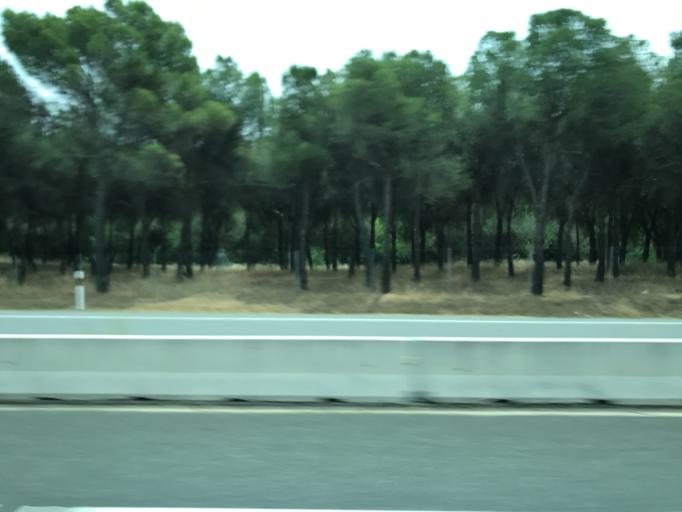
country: ES
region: Madrid
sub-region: Provincia de Madrid
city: San Agustin de Guadalix
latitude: 40.6836
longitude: -3.6102
